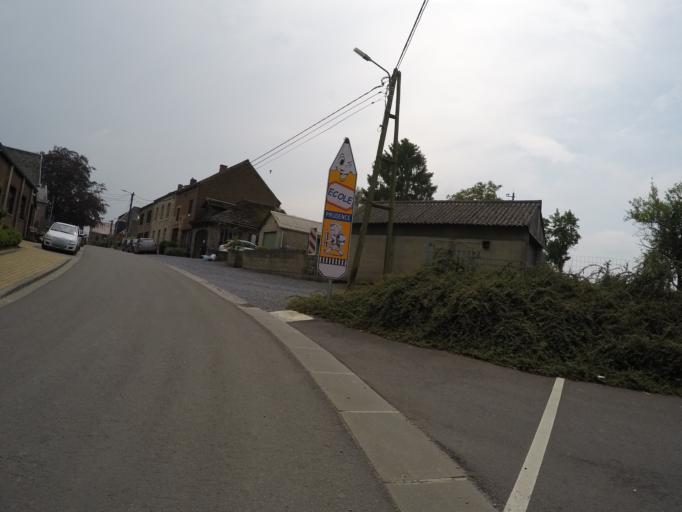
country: BE
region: Wallonia
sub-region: Province de Namur
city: Assesse
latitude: 50.3392
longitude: 4.9832
